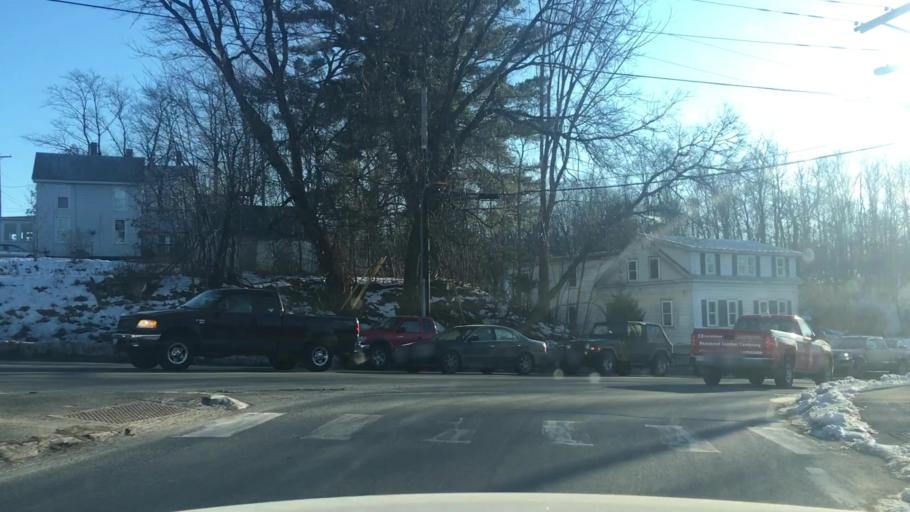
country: US
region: Maine
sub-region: Somerset County
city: Skowhegan
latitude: 44.7625
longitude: -69.7174
